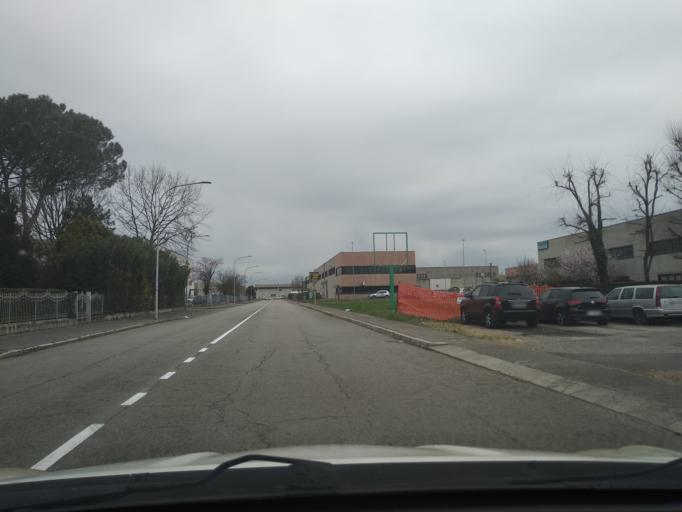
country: IT
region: Veneto
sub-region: Provincia di Padova
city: Rubano
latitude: 45.4213
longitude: 11.7950
